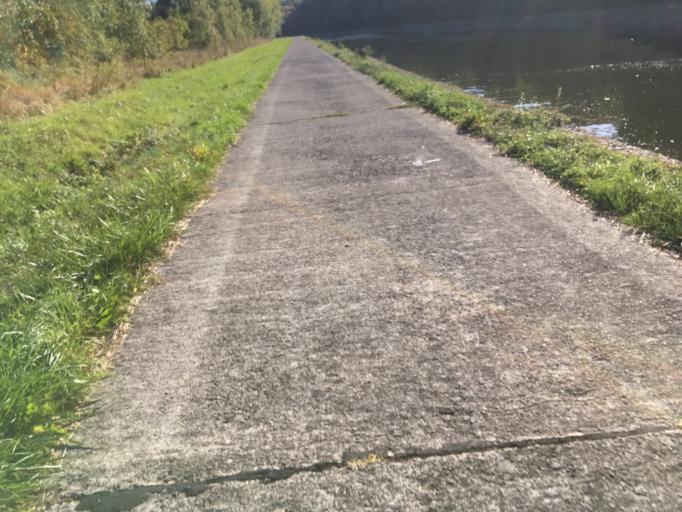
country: BE
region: Wallonia
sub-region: Province de Namur
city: Floreffe
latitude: 50.4453
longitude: 4.7606
